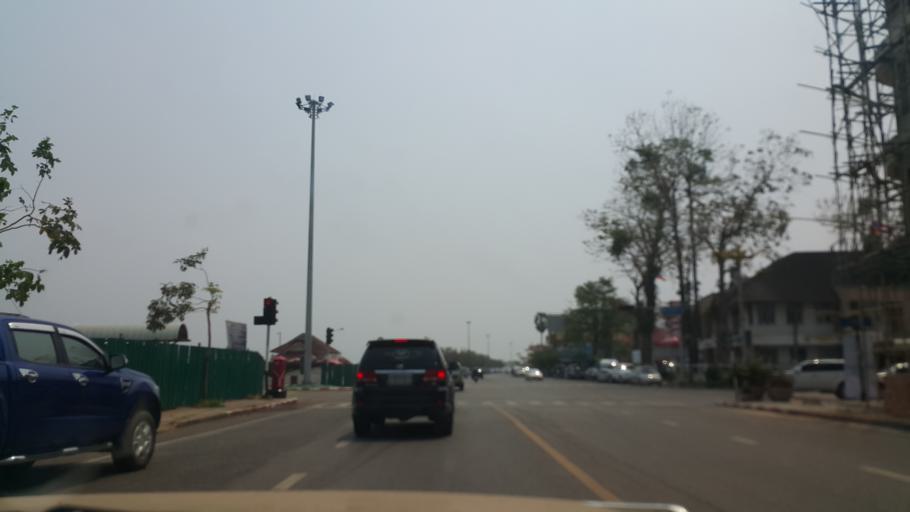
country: TH
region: Nakhon Phanom
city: Nakhon Phanom
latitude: 17.3996
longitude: 104.7901
